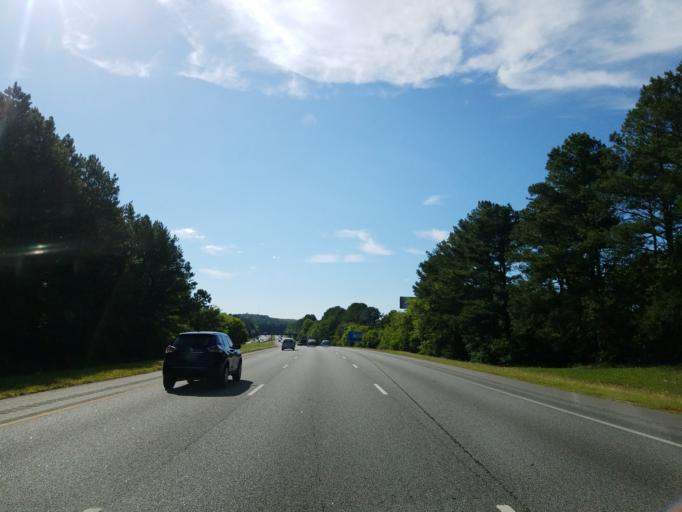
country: US
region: Georgia
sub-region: Bartow County
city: Cartersville
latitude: 34.2531
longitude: -84.7871
